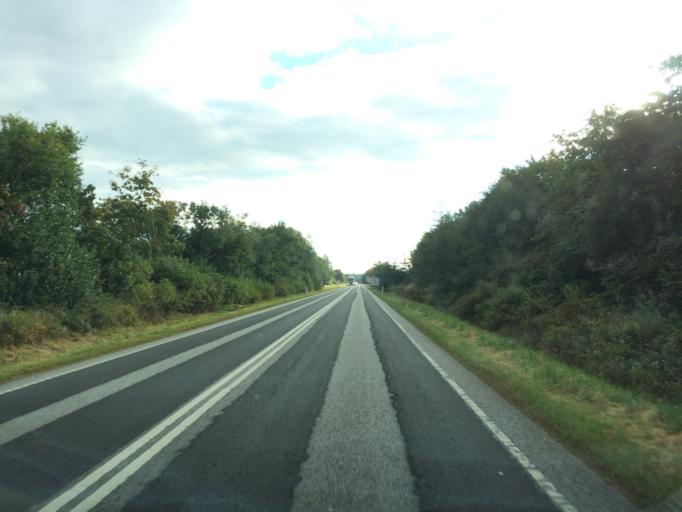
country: DK
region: Central Jutland
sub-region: Herning Kommune
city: Kibaek
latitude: 55.9453
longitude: 8.7753
